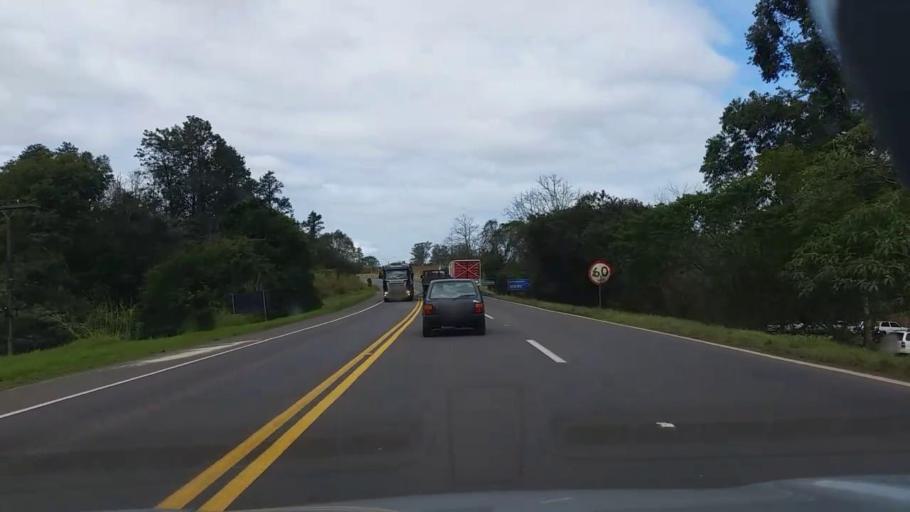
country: BR
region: Rio Grande do Sul
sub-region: Lajeado
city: Lajeado
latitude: -29.4264
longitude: -52.0193
